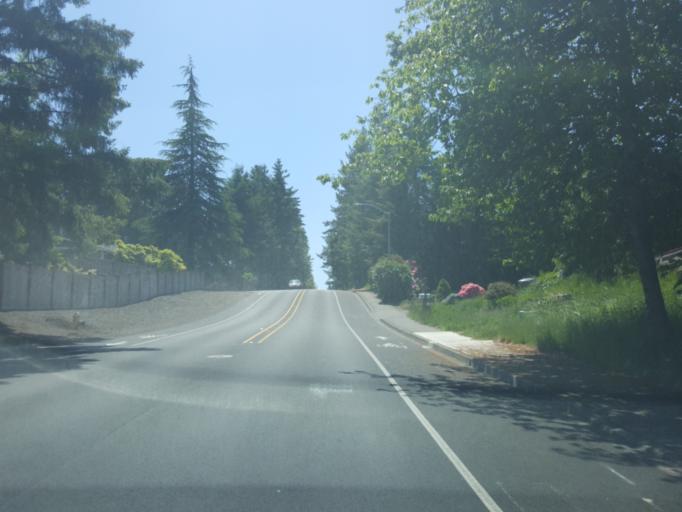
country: US
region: Washington
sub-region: Pierce County
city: Steilacoom
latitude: 47.1703
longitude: -122.5850
